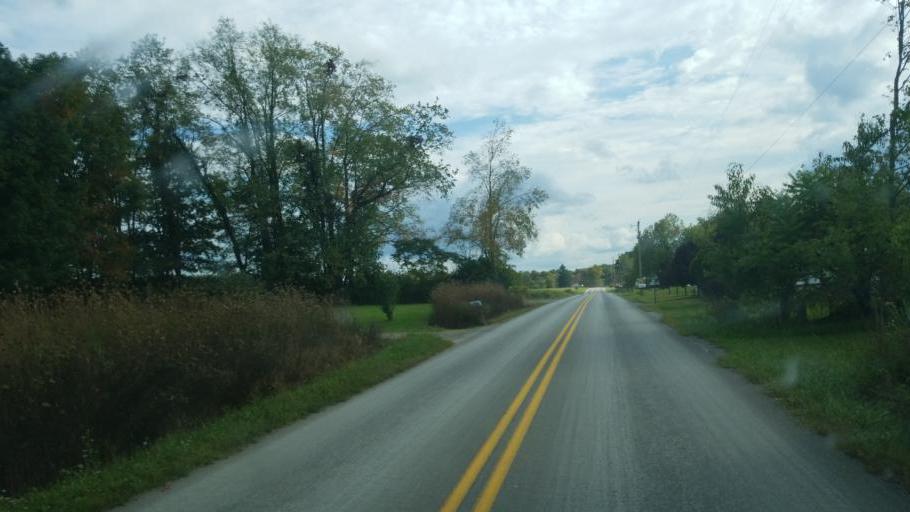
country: US
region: Pennsylvania
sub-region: Mercer County
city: Greenville
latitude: 41.4900
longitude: -80.3385
